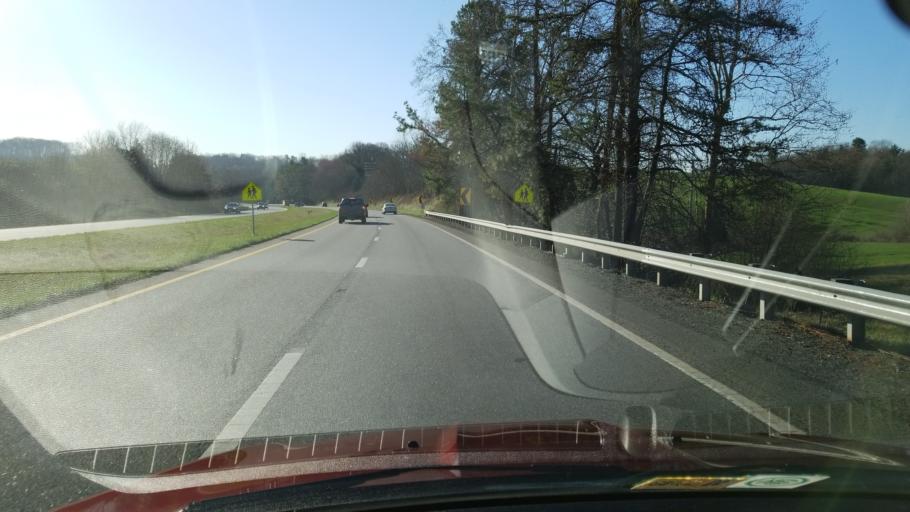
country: US
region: Virginia
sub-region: Franklin County
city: Rocky Mount
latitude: 37.0924
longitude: -79.9380
